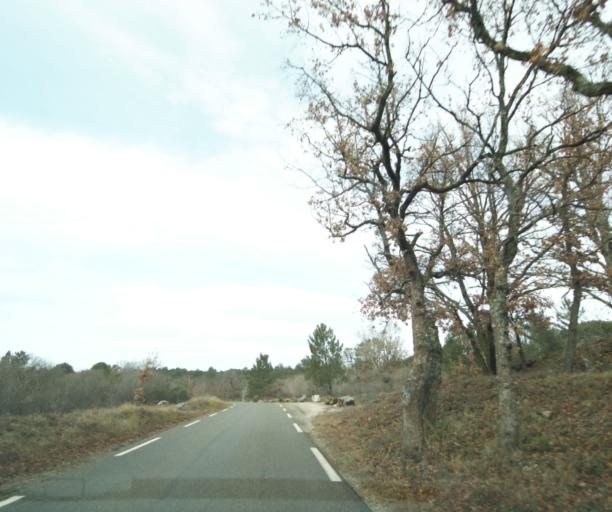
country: FR
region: Provence-Alpes-Cote d'Azur
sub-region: Departement du Var
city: Tourves
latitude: 43.3710
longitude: 5.9069
